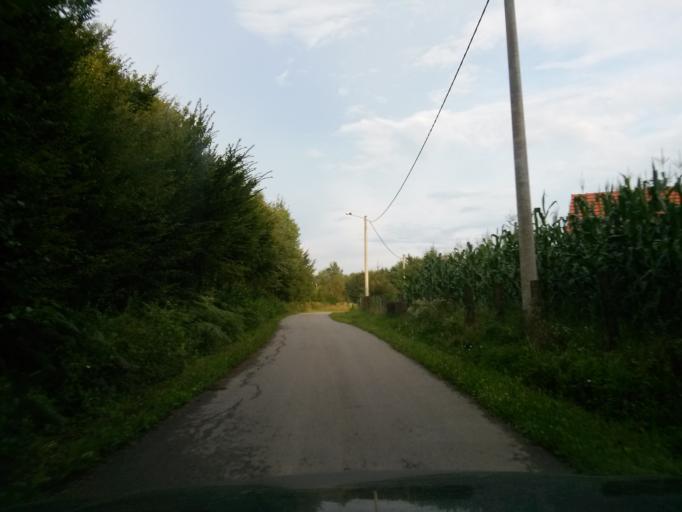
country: HR
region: Sisacko-Moslavacka
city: Gvozd
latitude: 45.2883
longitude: 15.9545
